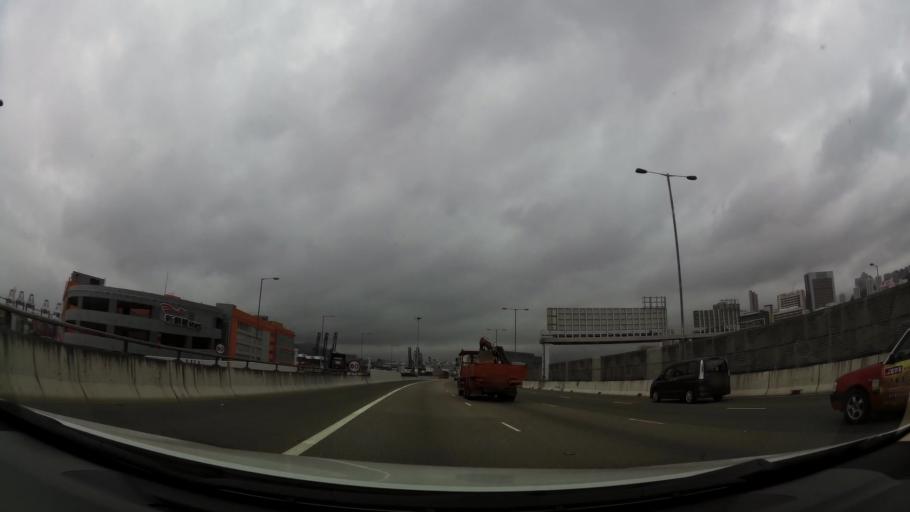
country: HK
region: Sham Shui Po
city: Sham Shui Po
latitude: 22.3344
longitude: 114.1358
